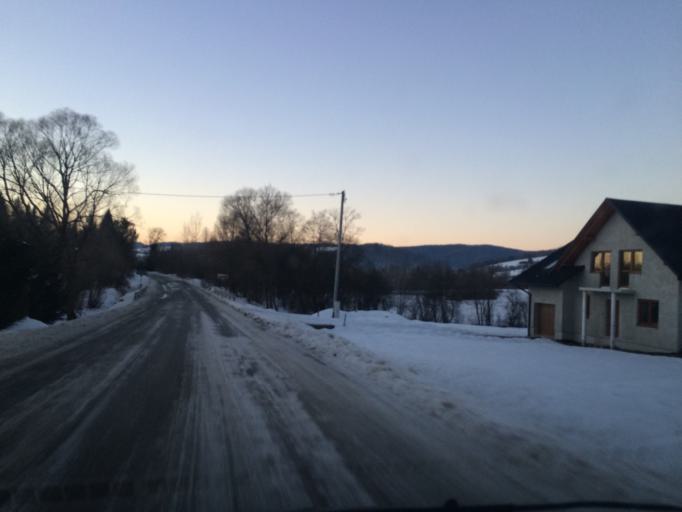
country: PL
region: Subcarpathian Voivodeship
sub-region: Powiat bieszczadzki
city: Ustrzyki Dolne
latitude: 49.4101
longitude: 22.5855
